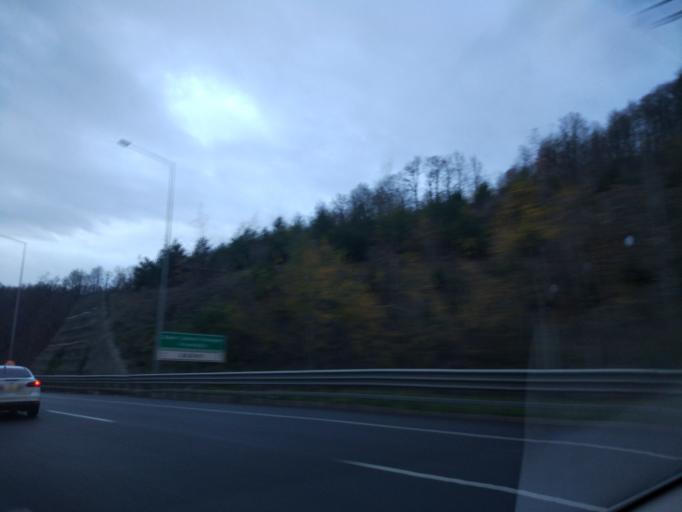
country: TR
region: Duzce
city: Kaynasli
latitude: 40.7586
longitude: 31.4441
